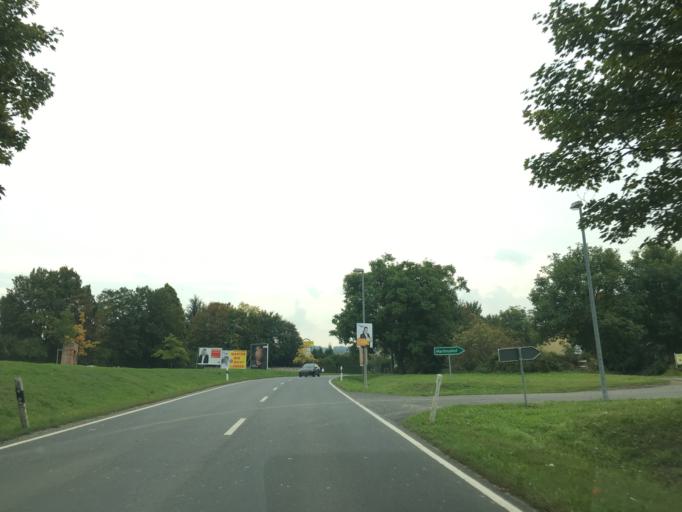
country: DE
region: Rheinland-Pfalz
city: Nieder-Olm
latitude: 49.9116
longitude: 8.1982
